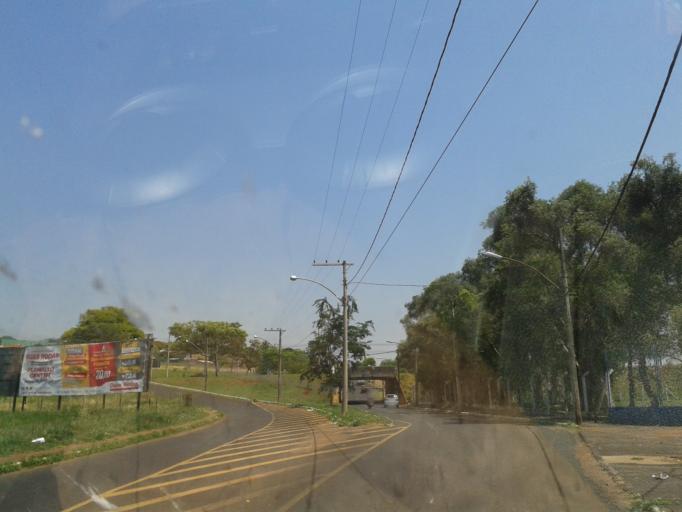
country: BR
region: Minas Gerais
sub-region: Uberlandia
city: Uberlandia
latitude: -18.9282
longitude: -48.2960
